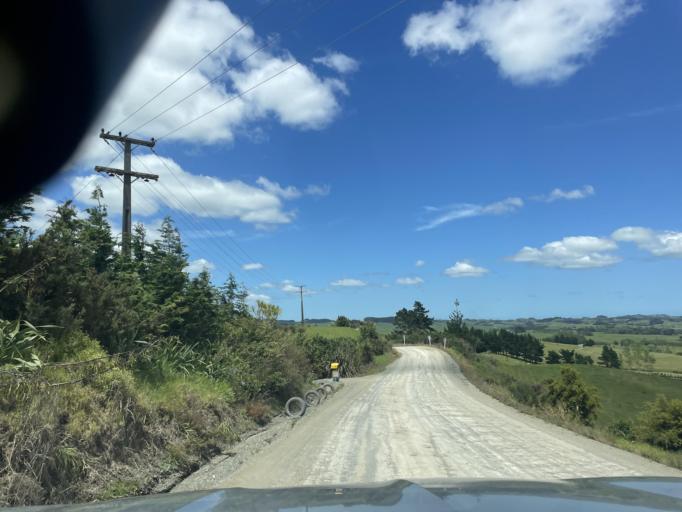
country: NZ
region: Auckland
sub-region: Auckland
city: Wellsford
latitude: -36.1356
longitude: 174.5363
